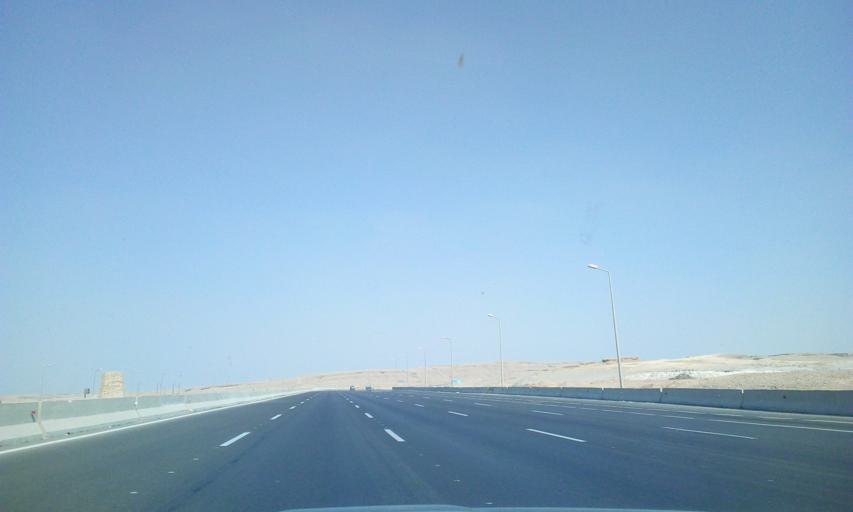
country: EG
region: As Suways
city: Ain Sukhna
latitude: 29.7607
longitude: 31.9947
